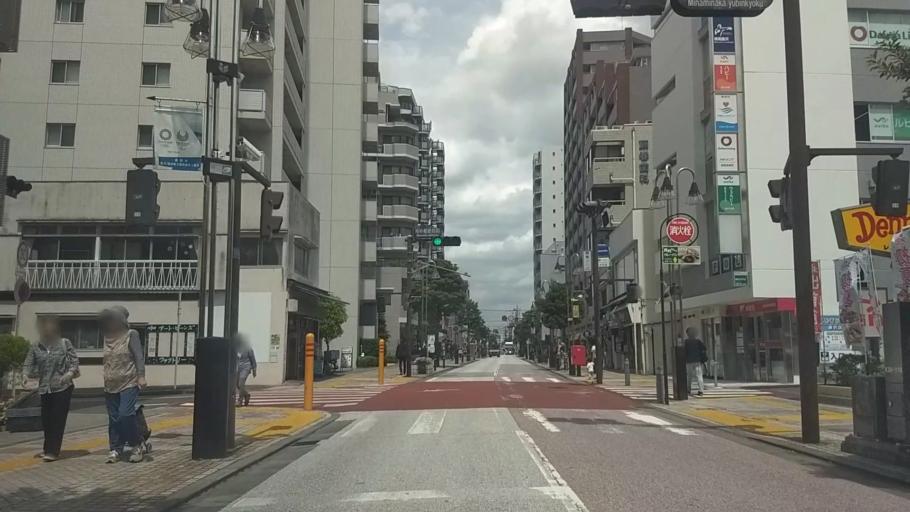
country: JP
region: Kanagawa
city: Fujisawa
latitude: 35.3413
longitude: 139.4838
